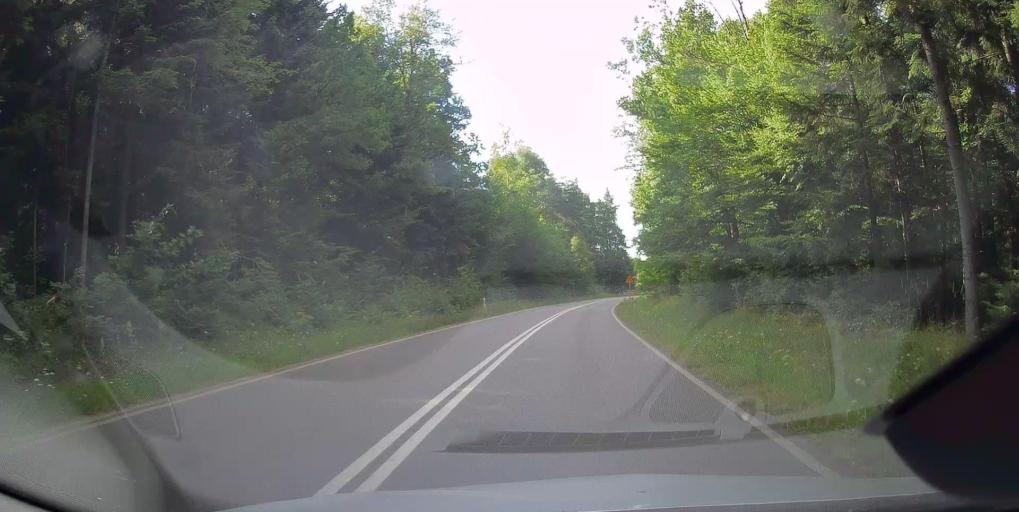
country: PL
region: Swietokrzyskie
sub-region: Powiat skarzyski
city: Laczna
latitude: 50.9962
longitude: 20.8530
